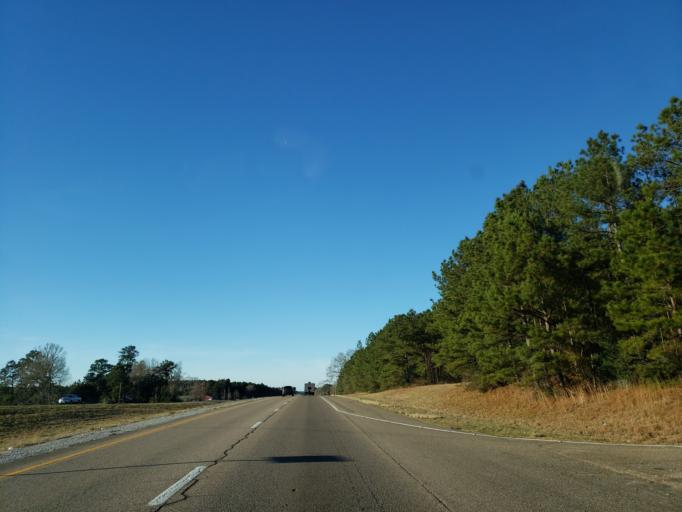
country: US
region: Mississippi
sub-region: Lamar County
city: Sumrall
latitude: 31.5026
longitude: -89.4750
